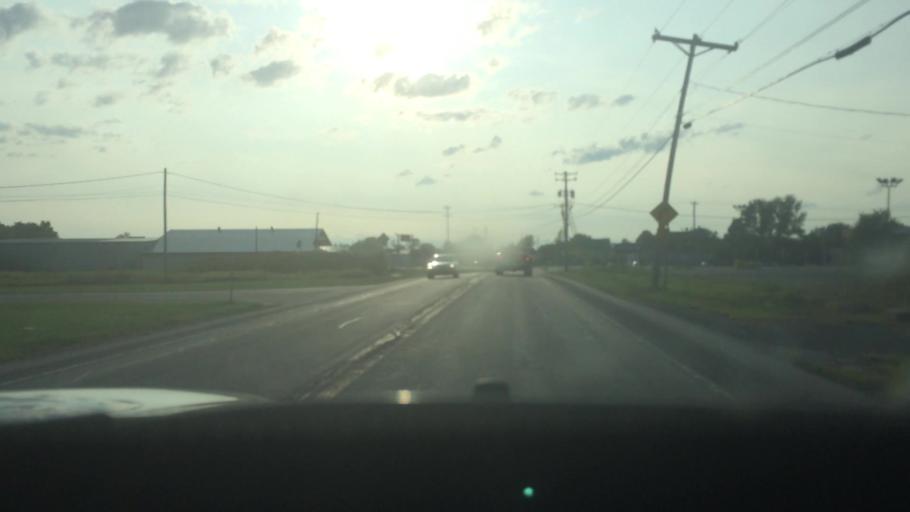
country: US
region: New York
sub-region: St. Lawrence County
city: Ogdensburg
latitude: 44.6895
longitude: -75.4723
